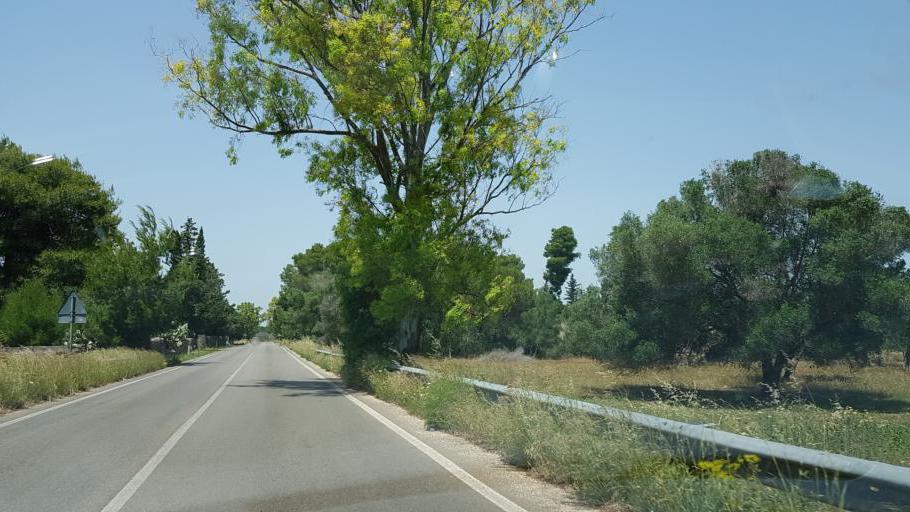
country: IT
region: Apulia
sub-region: Provincia di Lecce
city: Porto Cesareo
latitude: 40.2623
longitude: 17.9191
